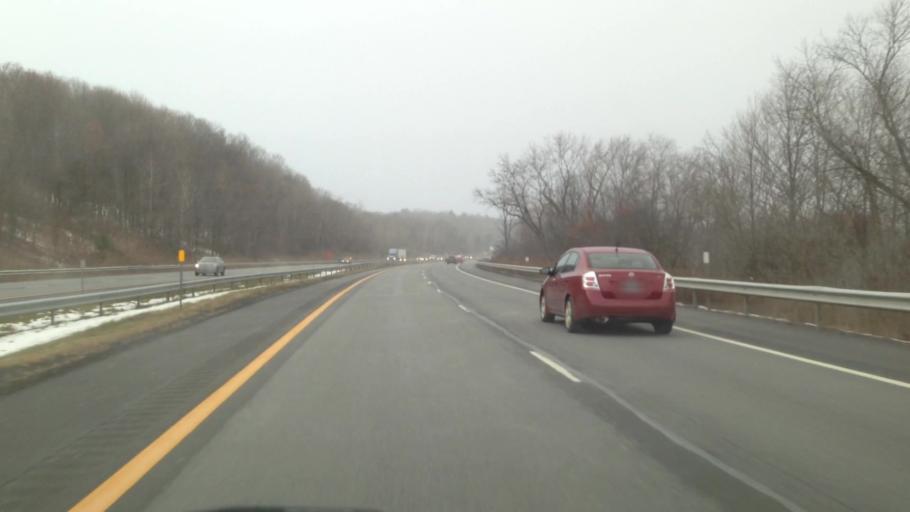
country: US
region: New York
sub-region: Schenectady County
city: Scotia
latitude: 42.8745
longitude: -74.0574
